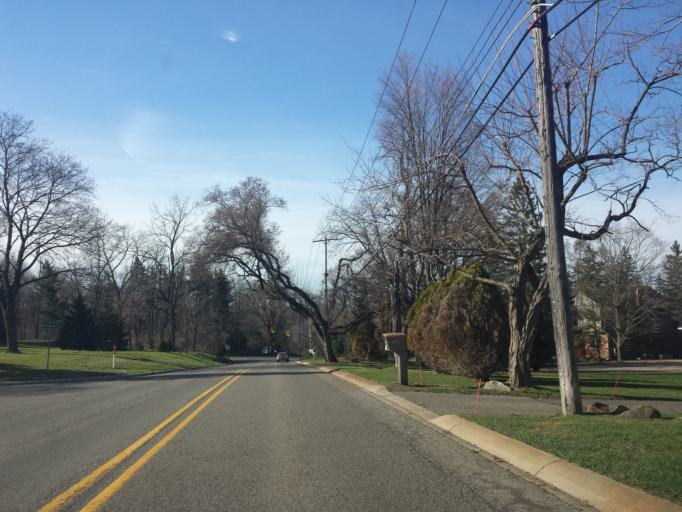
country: US
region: Michigan
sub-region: Oakland County
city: Franklin
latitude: 42.5162
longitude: -83.3056
